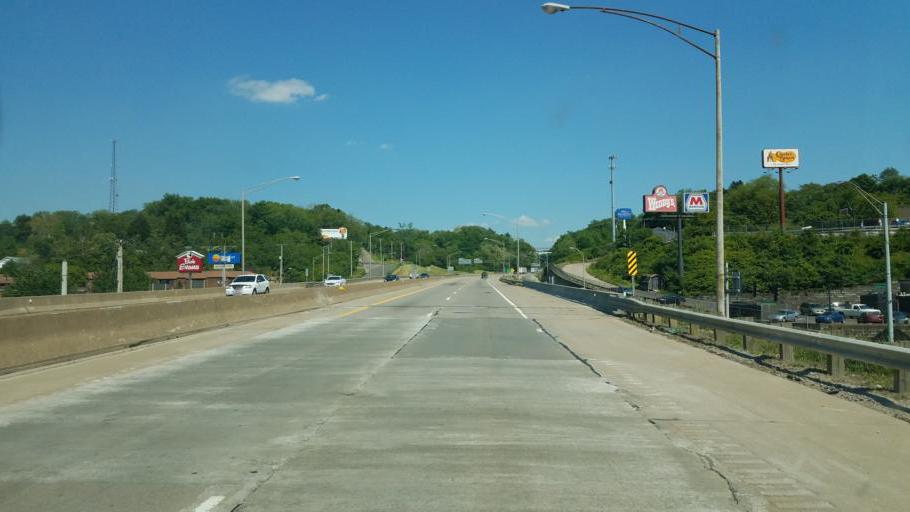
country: US
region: Ohio
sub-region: Muskingum County
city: Zanesville
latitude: 39.9446
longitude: -82.0019
